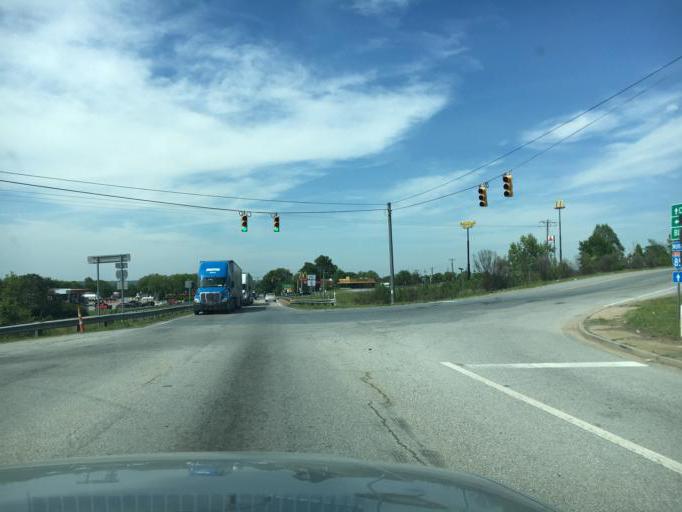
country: US
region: South Carolina
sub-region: Cherokee County
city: Blacksburg
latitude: 35.1399
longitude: -81.5087
